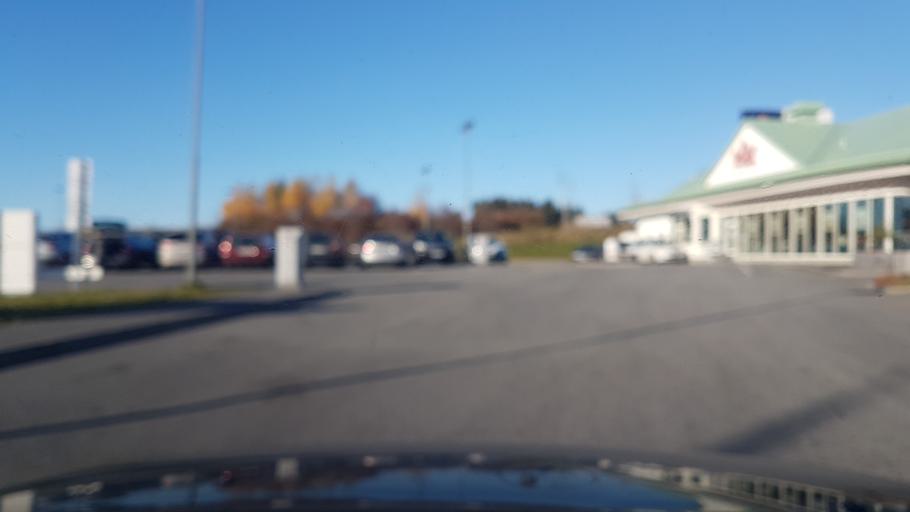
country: SE
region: Uppsala
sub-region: Uppsala Kommun
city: Gamla Uppsala
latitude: 59.8857
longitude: 17.6674
